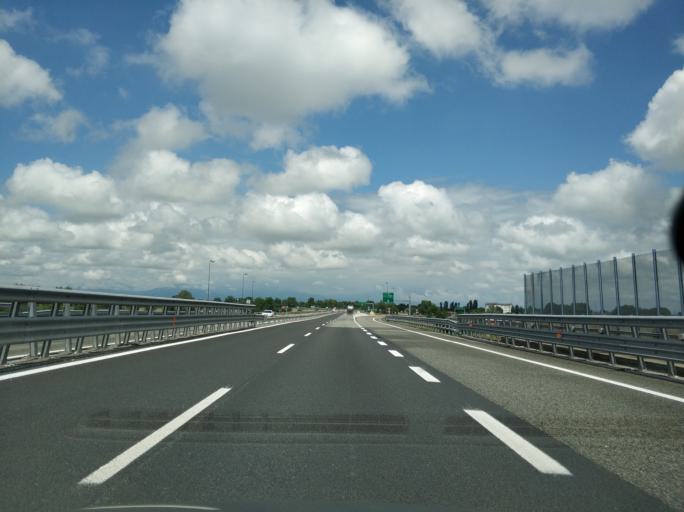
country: IT
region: Piedmont
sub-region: Provincia di Torino
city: Settimo Torinese
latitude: 45.1276
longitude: 7.7311
